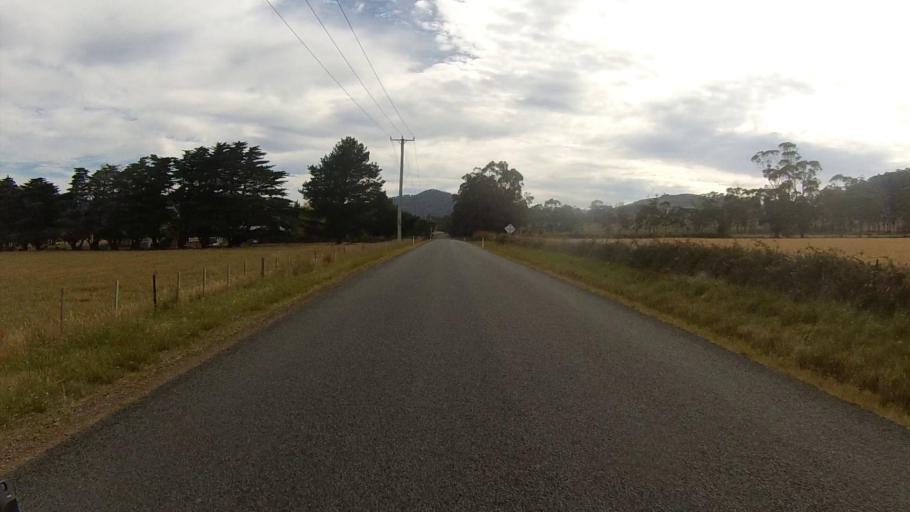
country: AU
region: Tasmania
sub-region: Sorell
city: Sorell
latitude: -42.7942
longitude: 147.7961
